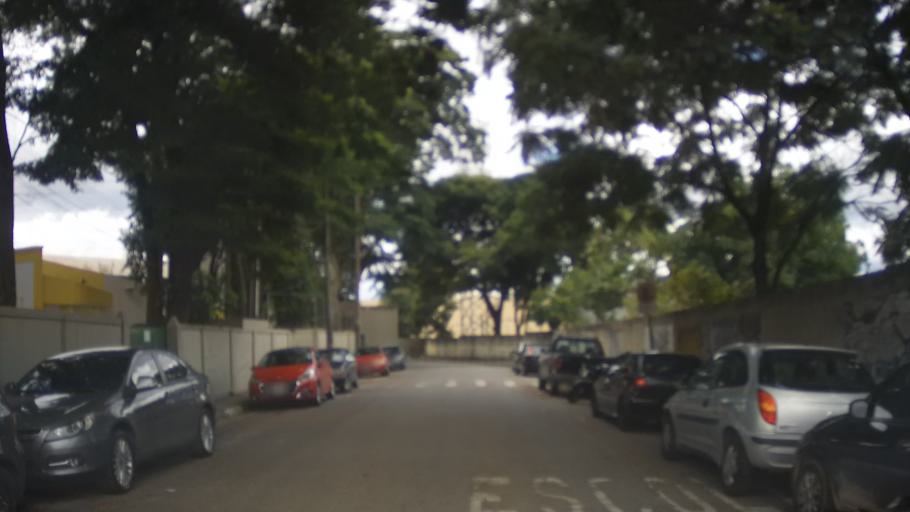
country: BR
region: Sao Paulo
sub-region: Guarulhos
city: Guarulhos
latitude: -23.4905
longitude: -46.5505
